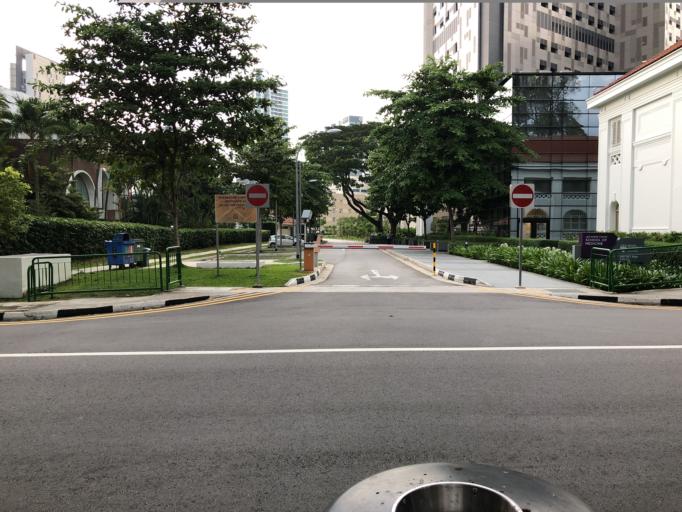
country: SG
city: Singapore
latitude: 1.3210
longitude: 103.8495
